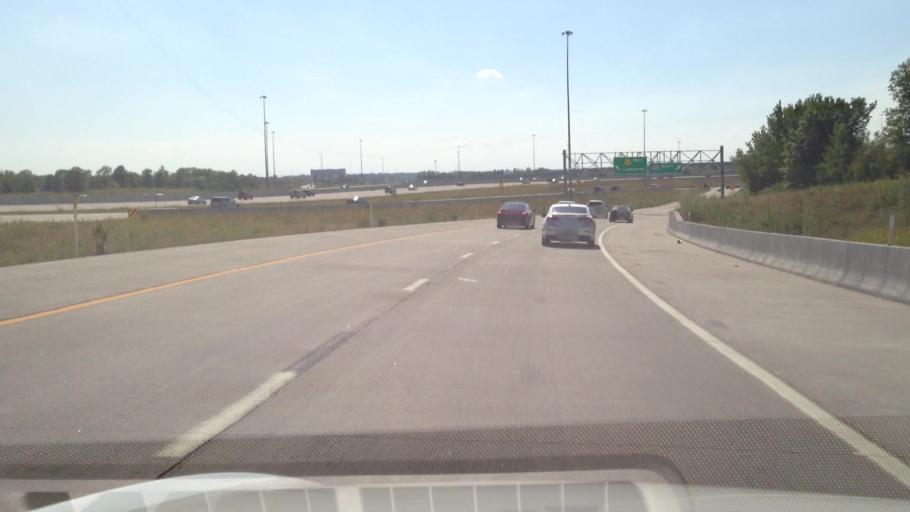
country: US
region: Kansas
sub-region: Johnson County
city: Lenexa
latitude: 38.9433
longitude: -94.7633
